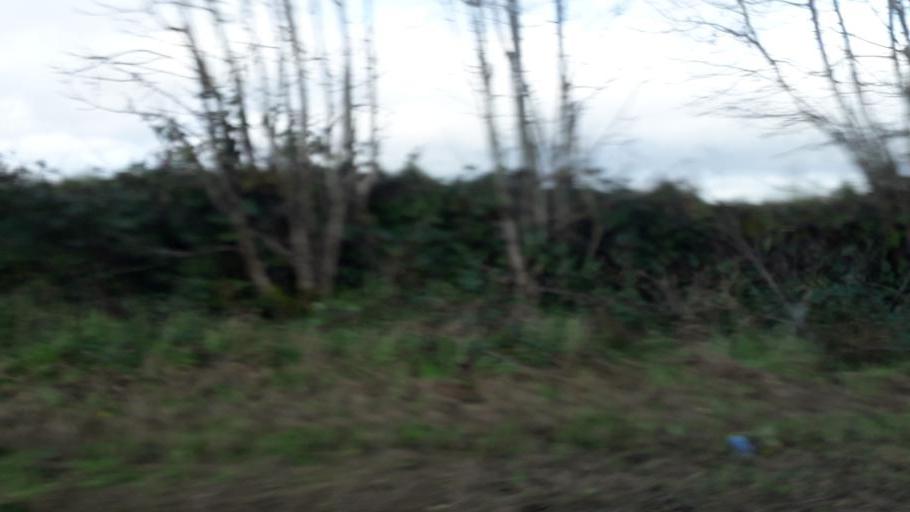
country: IE
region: Connaught
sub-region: Roscommon
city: Castlerea
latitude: 53.8808
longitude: -8.4446
